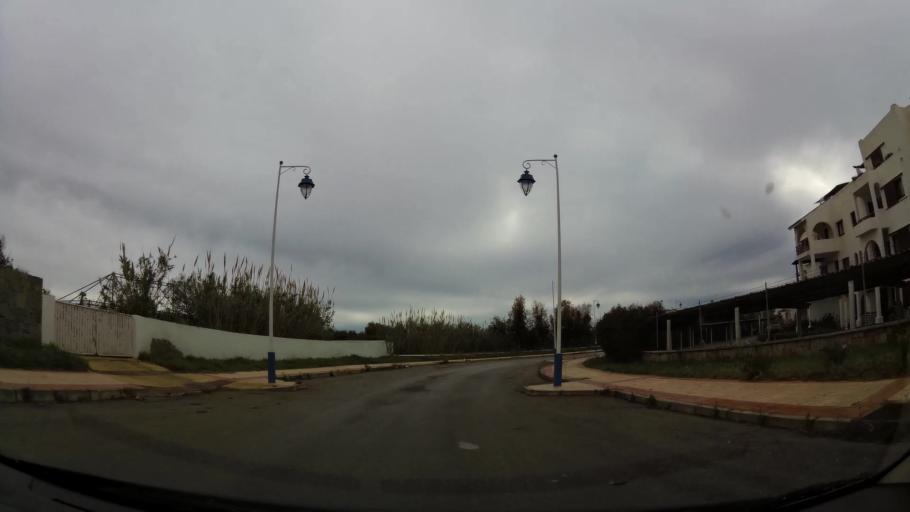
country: MA
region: Tanger-Tetouan
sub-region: Tetouan
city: Martil
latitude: 35.6626
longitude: -5.2882
